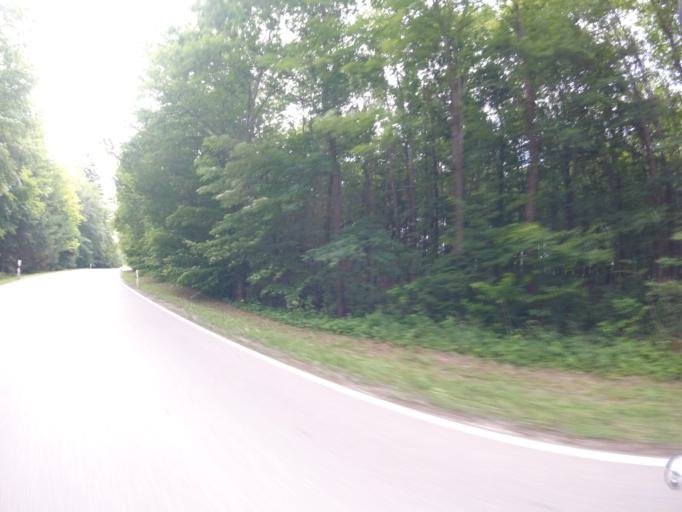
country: DE
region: Bavaria
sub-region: Upper Bavaria
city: Paunzhausen
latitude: 48.4803
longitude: 11.5477
